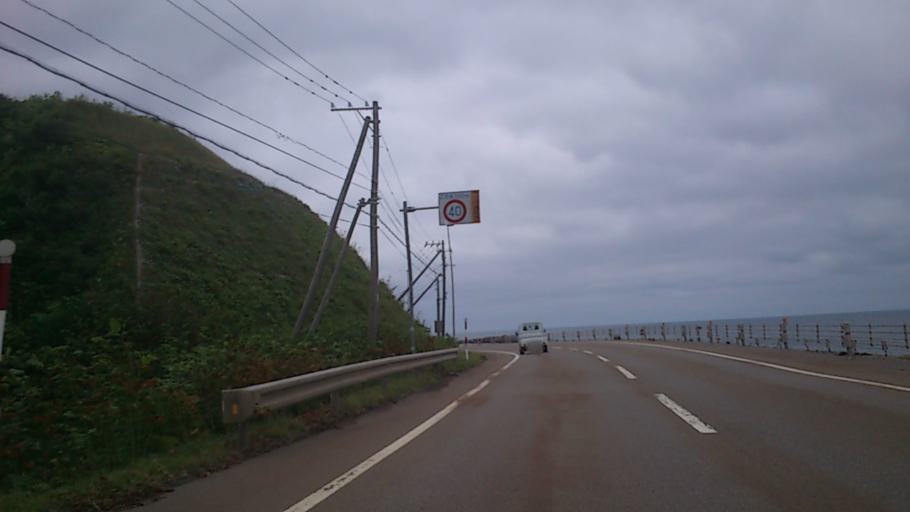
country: JP
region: Hokkaido
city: Kamiiso
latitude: 41.7113
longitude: 140.0276
